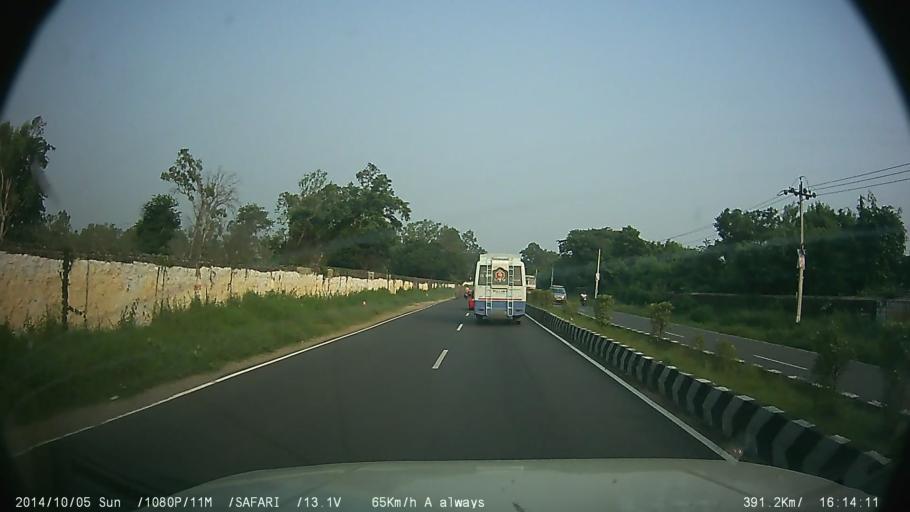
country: IN
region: Tamil Nadu
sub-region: Kancheepuram
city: Vandalur
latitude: 12.8740
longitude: 80.0915
